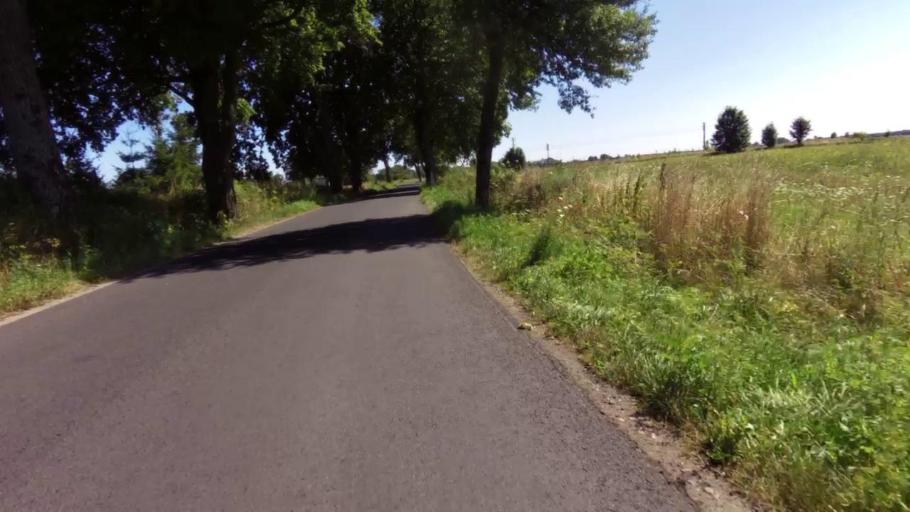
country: PL
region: West Pomeranian Voivodeship
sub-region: Powiat drawski
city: Czaplinek
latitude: 53.5575
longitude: 16.3150
